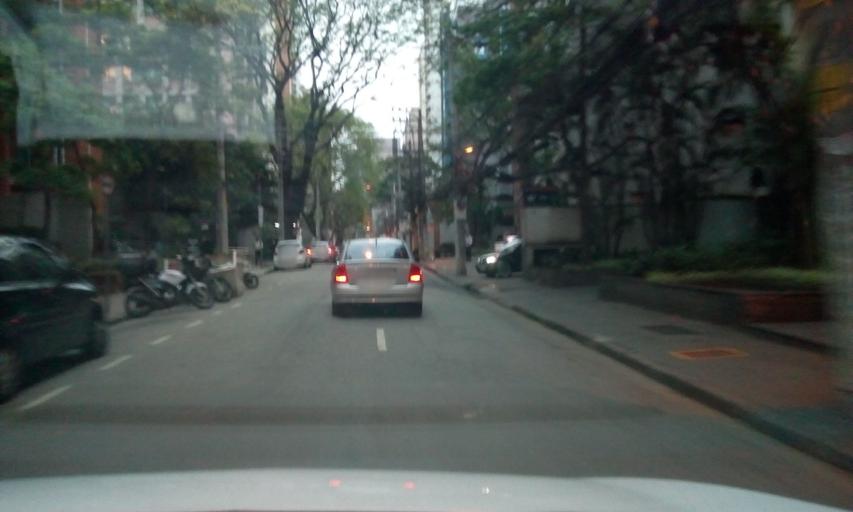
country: BR
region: Sao Paulo
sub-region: Sao Paulo
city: Sao Paulo
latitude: -23.5944
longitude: -46.6869
